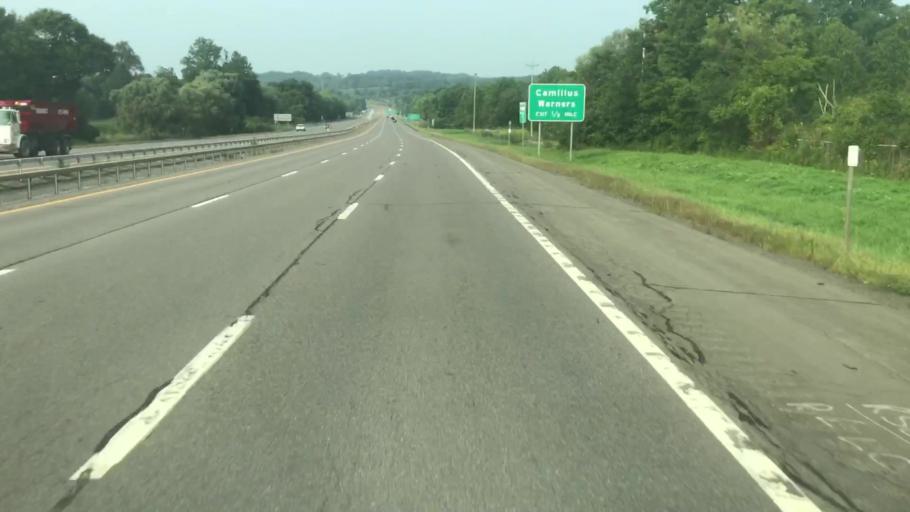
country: US
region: New York
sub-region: Onondaga County
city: Camillus
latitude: 43.0535
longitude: -76.2904
